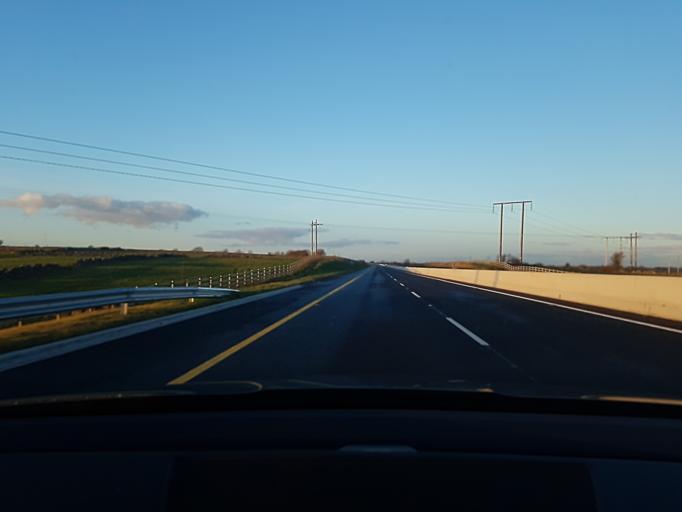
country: IE
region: Connaught
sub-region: County Galway
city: Tuam
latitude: 53.4772
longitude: -8.8638
